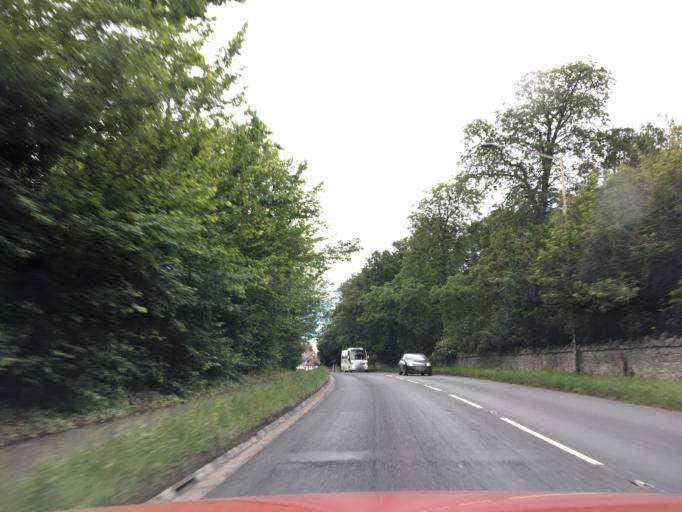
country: GB
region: England
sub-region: Buckinghamshire
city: Stone
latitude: 51.8034
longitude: -0.8522
